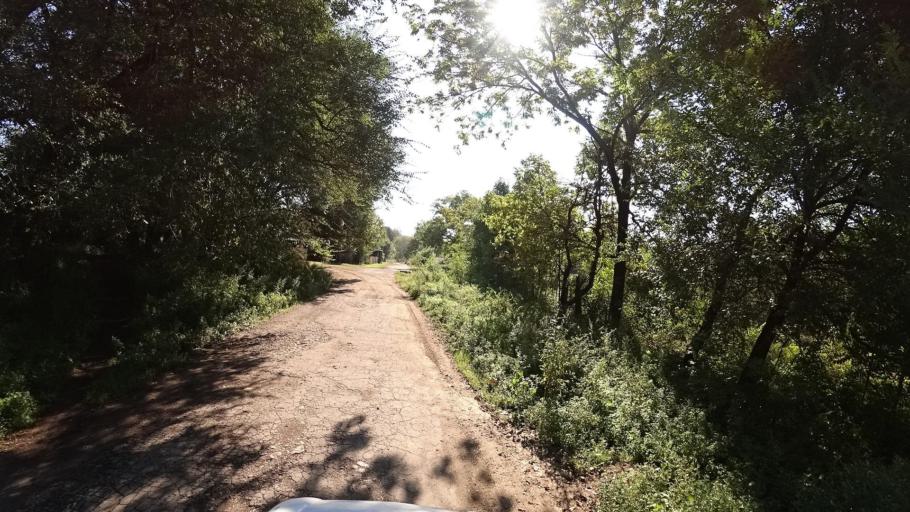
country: RU
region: Jewish Autonomous Oblast
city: Bira
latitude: 49.0012
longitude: 132.4665
